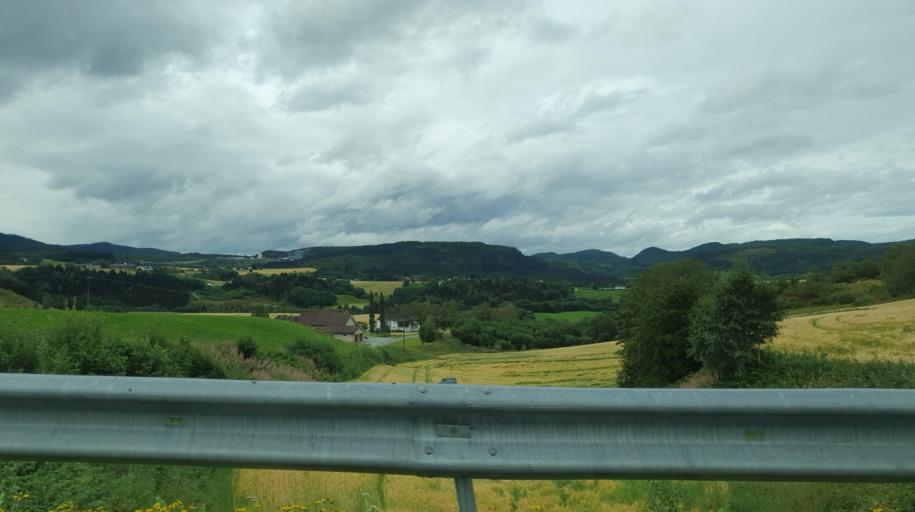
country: NO
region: Nord-Trondelag
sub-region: Stjordal
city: Stjordalshalsen
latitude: 63.4209
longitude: 10.9600
